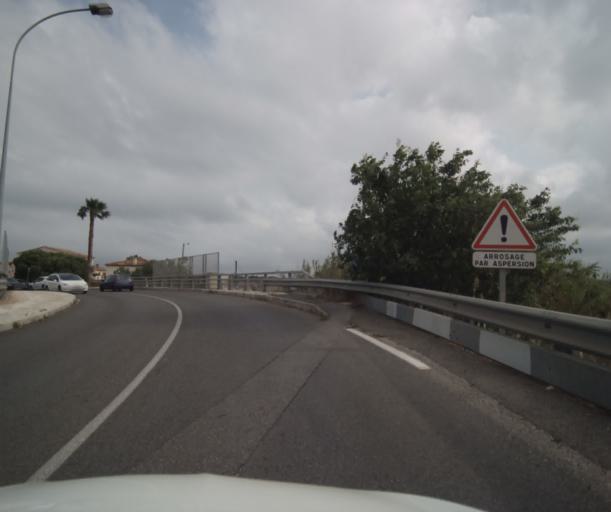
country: FR
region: Provence-Alpes-Cote d'Azur
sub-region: Departement du Var
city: La Seyne-sur-Mer
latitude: 43.1210
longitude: 5.8801
